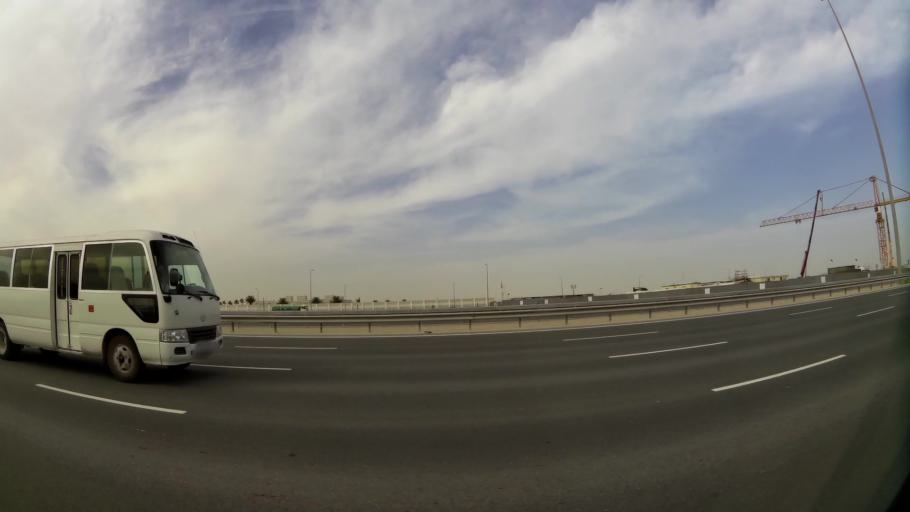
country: QA
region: Baladiyat ar Rayyan
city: Ar Rayyan
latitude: 25.3151
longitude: 51.3696
